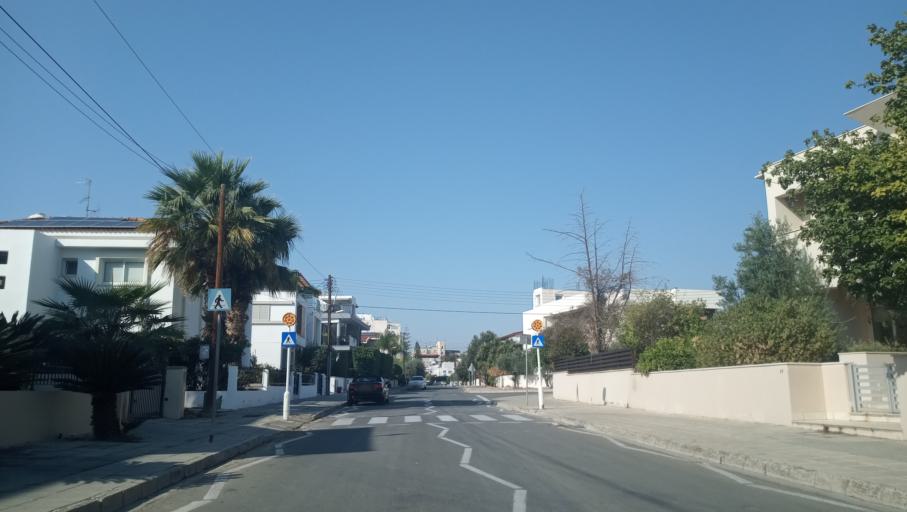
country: CY
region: Lefkosia
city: Nicosia
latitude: 35.1429
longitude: 33.3861
